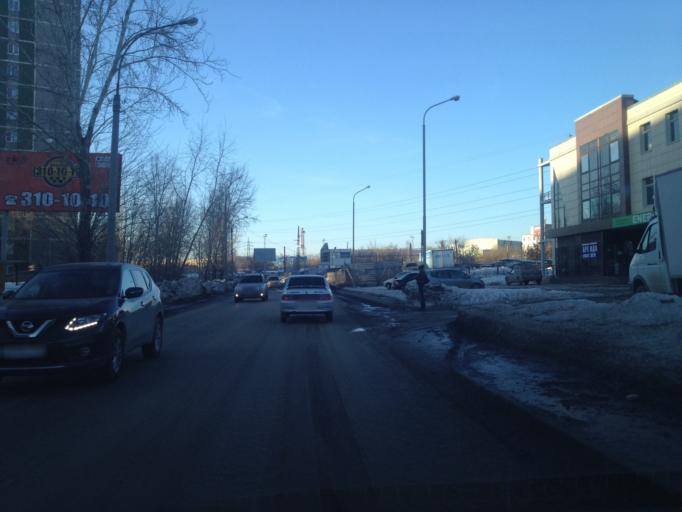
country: RU
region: Sverdlovsk
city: Yekaterinburg
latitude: 56.8681
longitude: 60.5651
